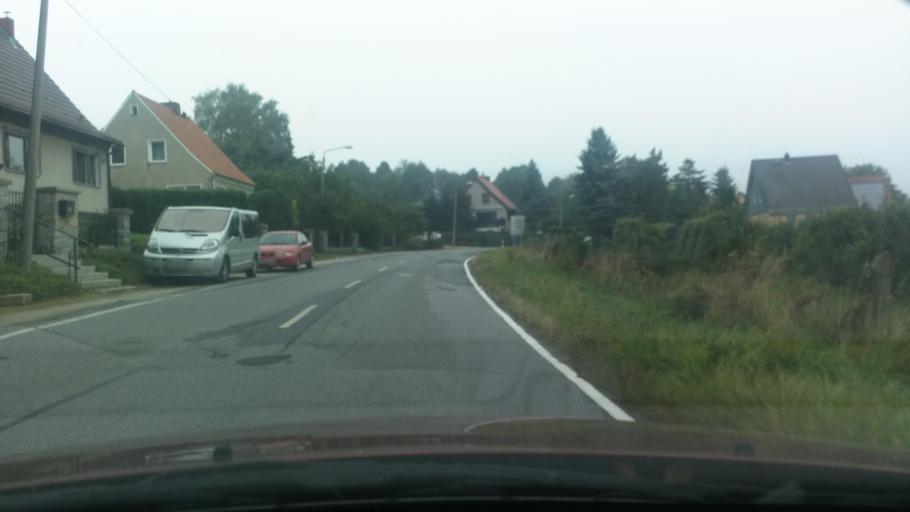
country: DE
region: Saxony
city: Goerlitz
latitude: 51.1279
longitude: 14.9411
